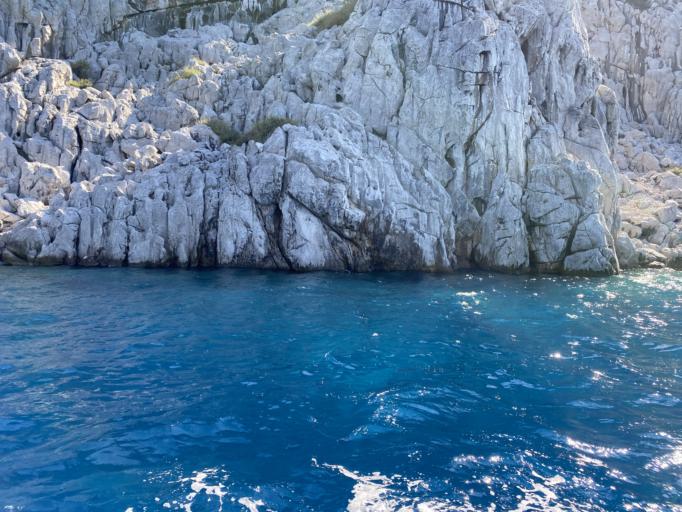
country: TR
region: Mugla
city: Bozburun
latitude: 36.7285
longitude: 28.0871
